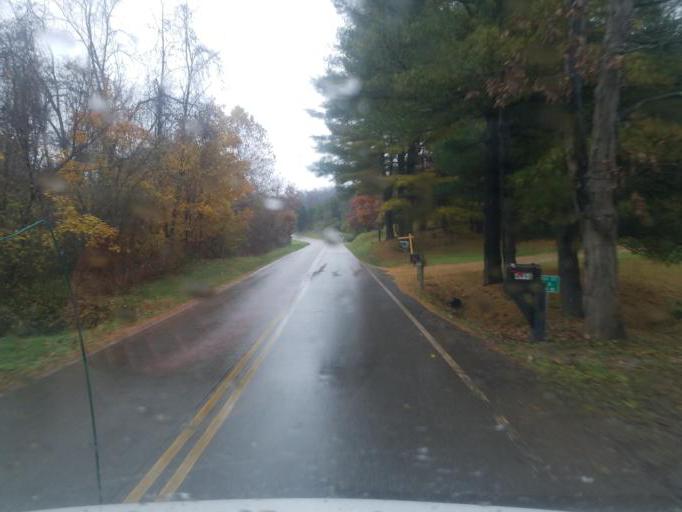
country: US
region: West Virginia
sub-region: Wood County
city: Blennerhassett
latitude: 39.3285
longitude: -81.6211
